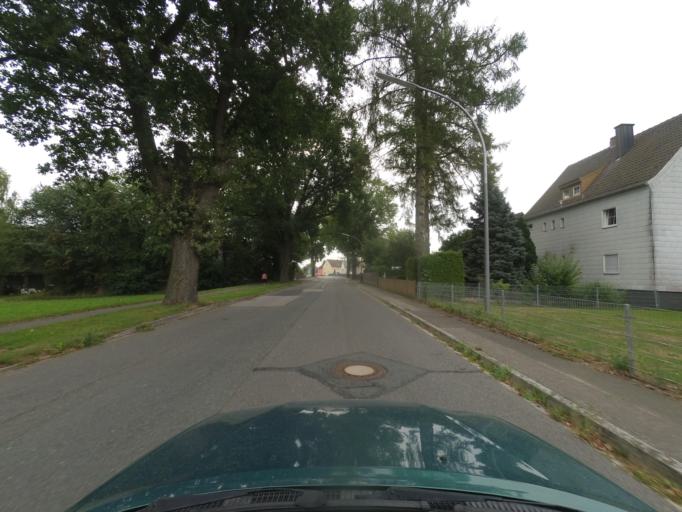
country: DE
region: Bavaria
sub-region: Upper Palatinate
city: Eslarn
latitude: 49.5821
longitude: 12.5105
